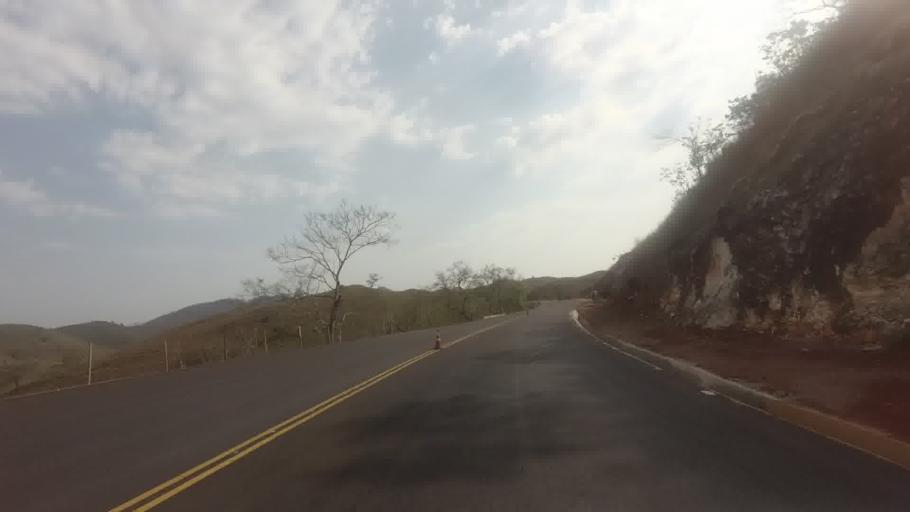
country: BR
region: Rio de Janeiro
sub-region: Itaperuna
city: Itaperuna
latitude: -21.2896
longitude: -41.8019
